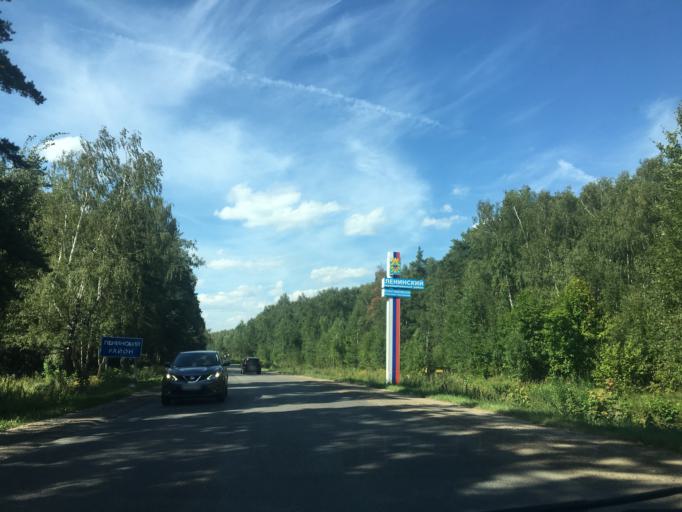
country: RU
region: Moskovskaya
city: Vidnoye
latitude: 55.5210
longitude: 37.6810
